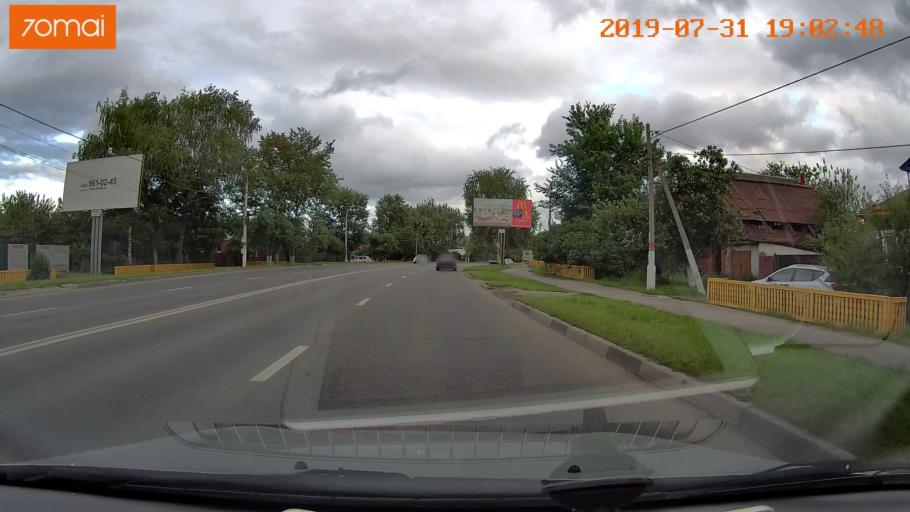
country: RU
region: Moskovskaya
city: Raduzhnyy
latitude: 55.1187
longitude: 38.7346
